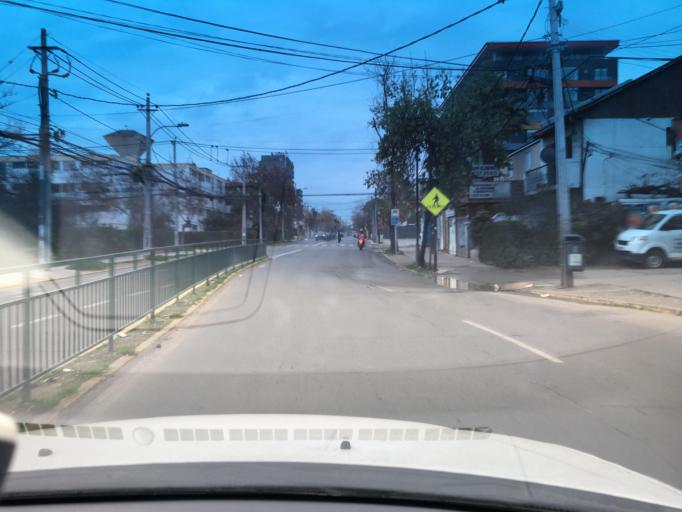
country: CL
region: Santiago Metropolitan
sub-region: Provincia de Santiago
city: Villa Presidente Frei, Nunoa, Santiago, Chile
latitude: -33.4619
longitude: -70.6061
